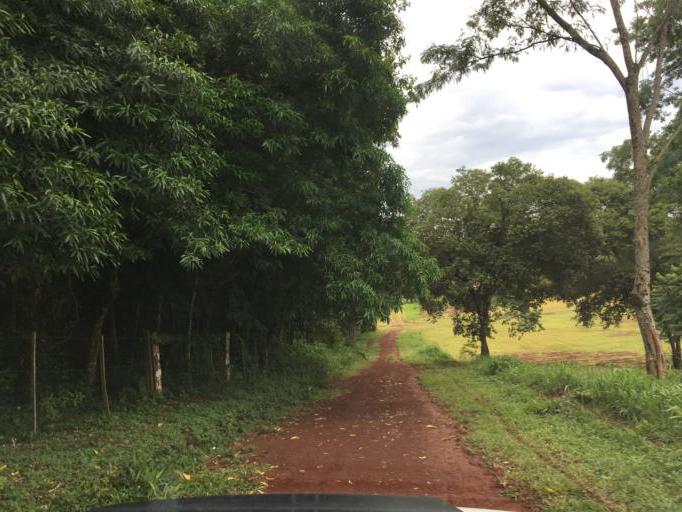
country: PY
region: Alto Parana
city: Ciudad del Este
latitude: -25.4113
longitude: -54.6527
